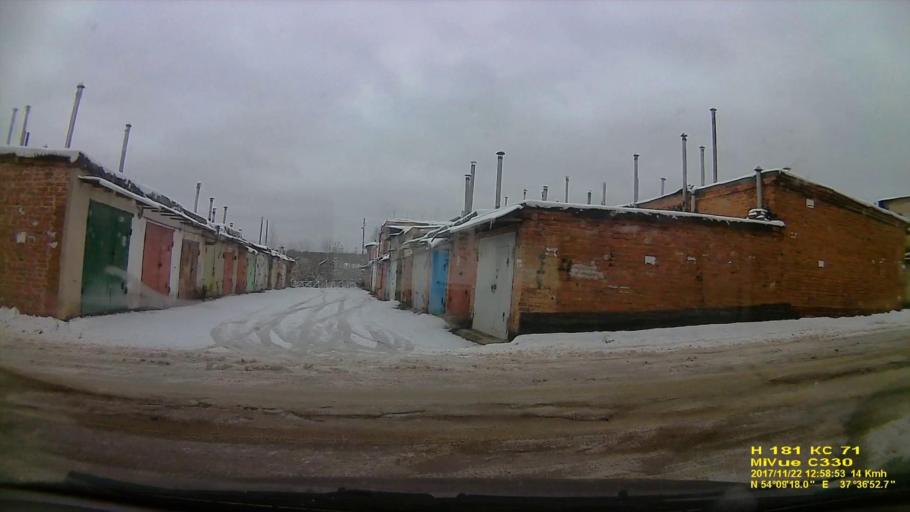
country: RU
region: Tula
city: Mendeleyevskiy
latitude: 54.1550
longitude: 37.6145
